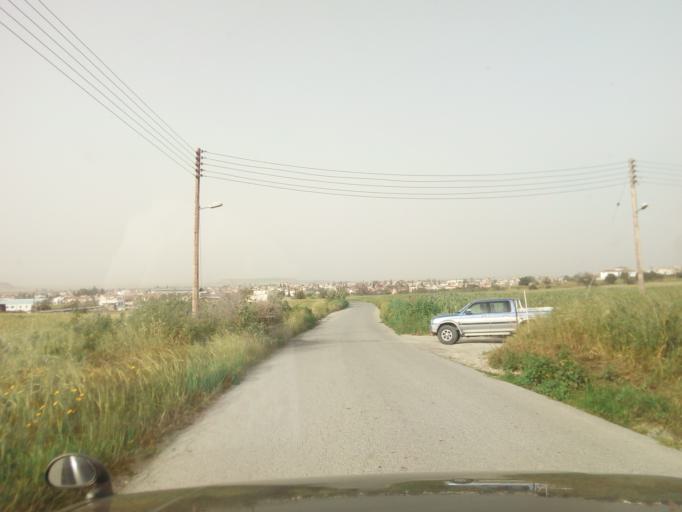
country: CY
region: Larnaka
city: Athienou
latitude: 35.0487
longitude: 33.5363
